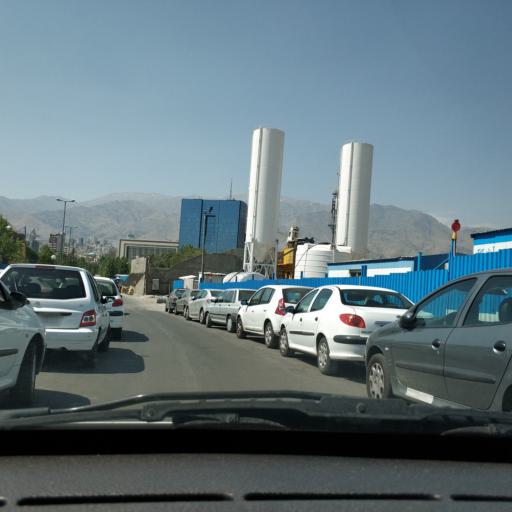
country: IR
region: Tehran
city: Tajrish
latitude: 35.7532
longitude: 51.4357
